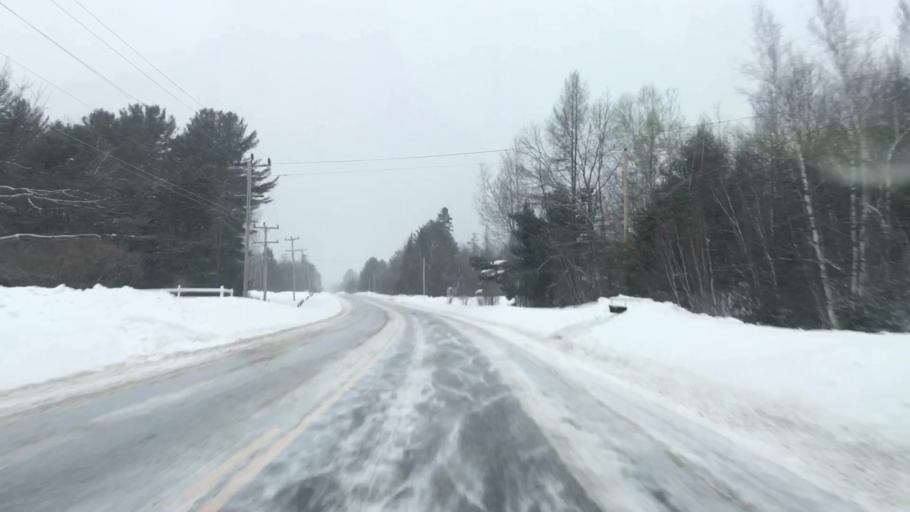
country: US
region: Maine
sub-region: Penobscot County
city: Medway
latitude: 45.5430
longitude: -68.3703
